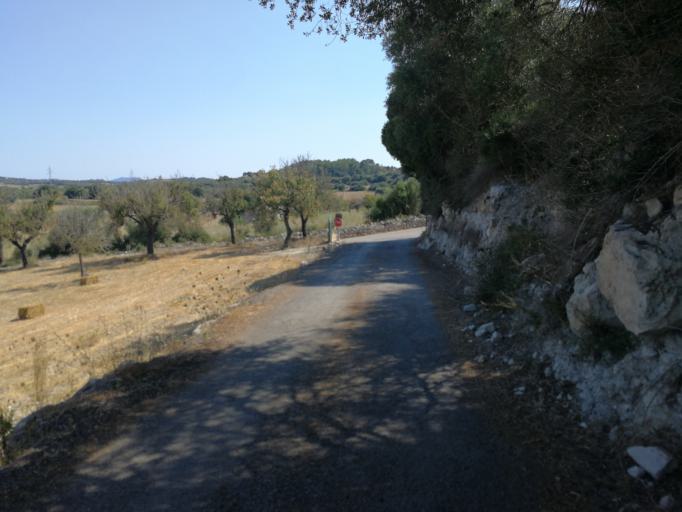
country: ES
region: Balearic Islands
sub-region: Illes Balears
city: Muro
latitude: 39.7347
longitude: 3.0738
